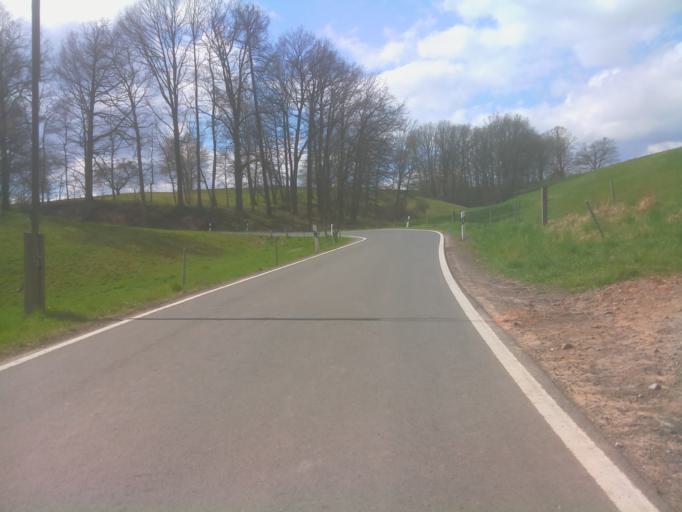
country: DE
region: Thuringia
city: Karlsdorf
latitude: 50.7942
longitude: 11.8002
